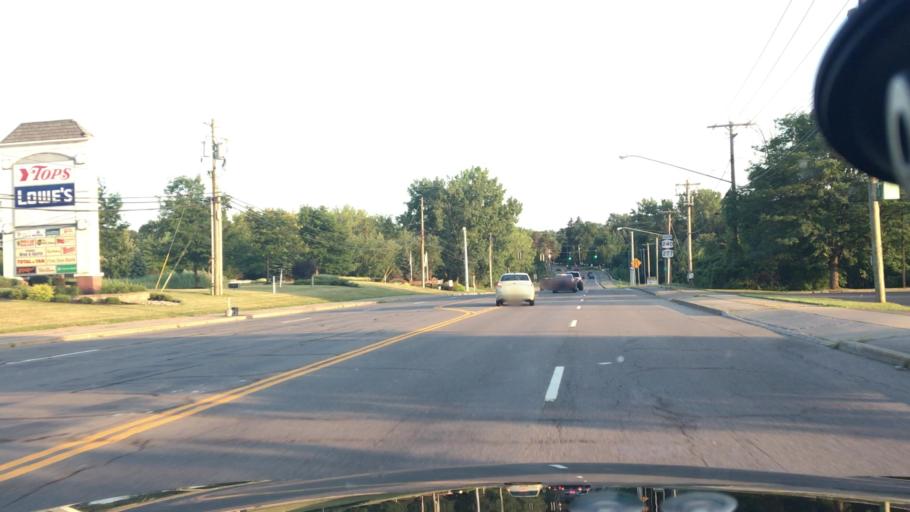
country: US
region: New York
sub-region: Erie County
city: Orchard Park
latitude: 42.7958
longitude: -78.7518
